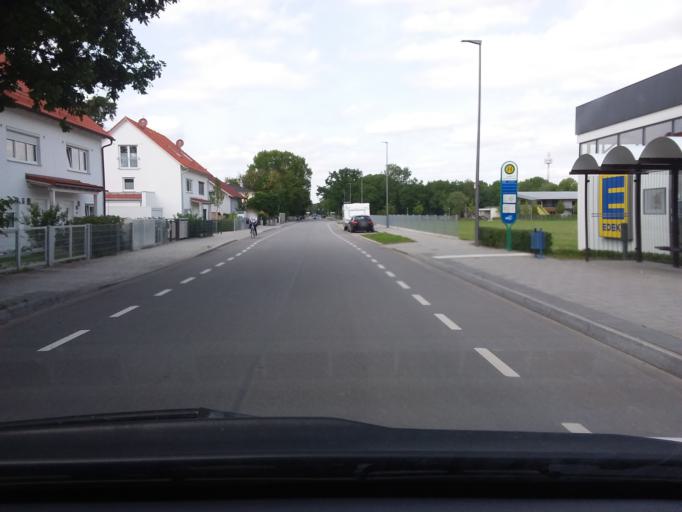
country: DE
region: Bavaria
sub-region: Upper Bavaria
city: Unterschleissheim
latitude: 48.2777
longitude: 11.5888
